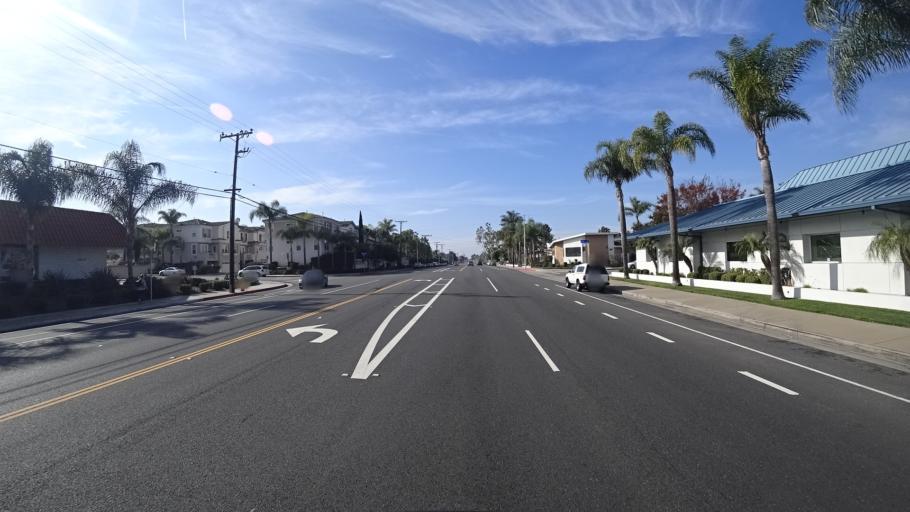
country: US
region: California
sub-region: Orange County
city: Fountain Valley
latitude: 33.7012
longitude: -117.9902
